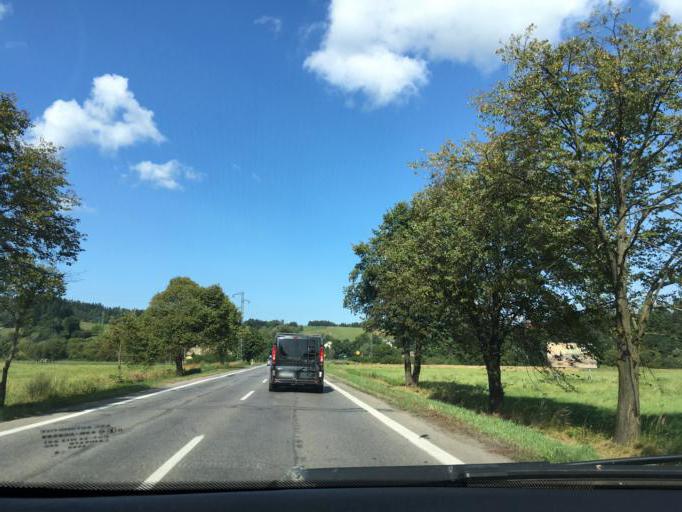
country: PL
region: Subcarpathian Voivodeship
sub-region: Powiat leski
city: Lesko
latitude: 49.4931
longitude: 22.3148
